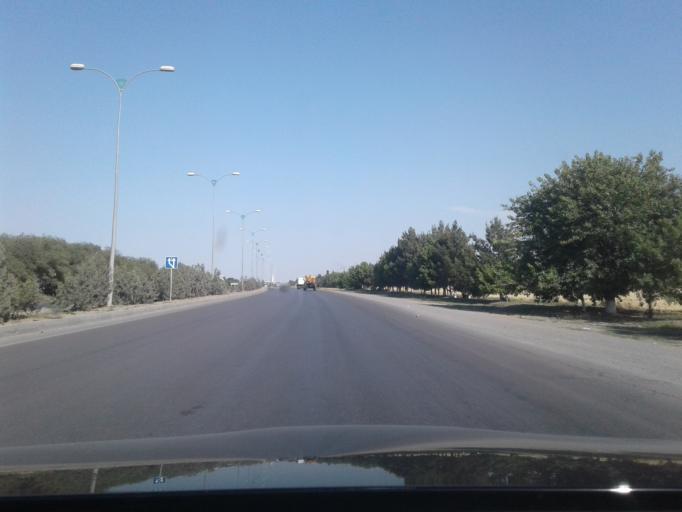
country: TM
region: Ahal
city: Abadan
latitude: 38.1060
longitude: 58.0670
